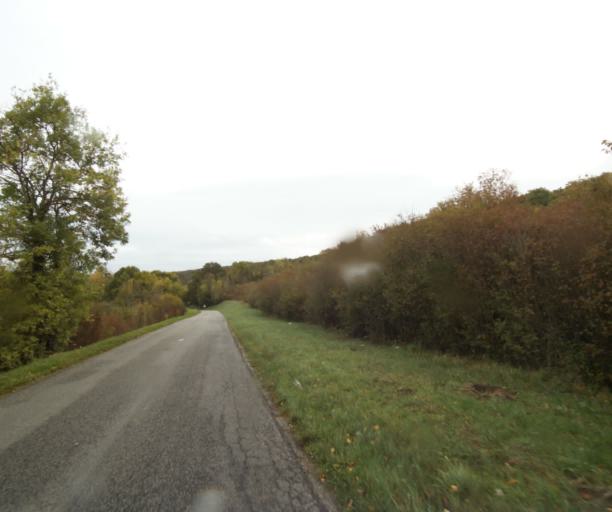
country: FR
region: Centre
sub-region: Departement d'Eure-et-Loir
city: Vert-en-Drouais
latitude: 48.7593
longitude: 1.3264
